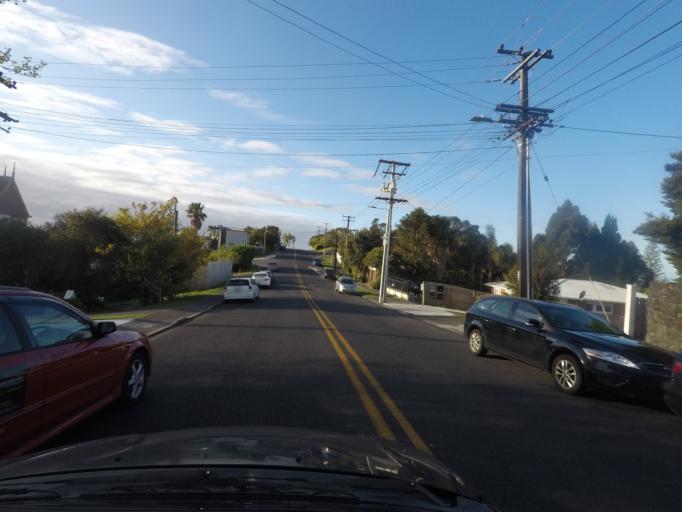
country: NZ
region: Auckland
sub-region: Auckland
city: Waitakere
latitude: -36.9187
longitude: 174.6580
